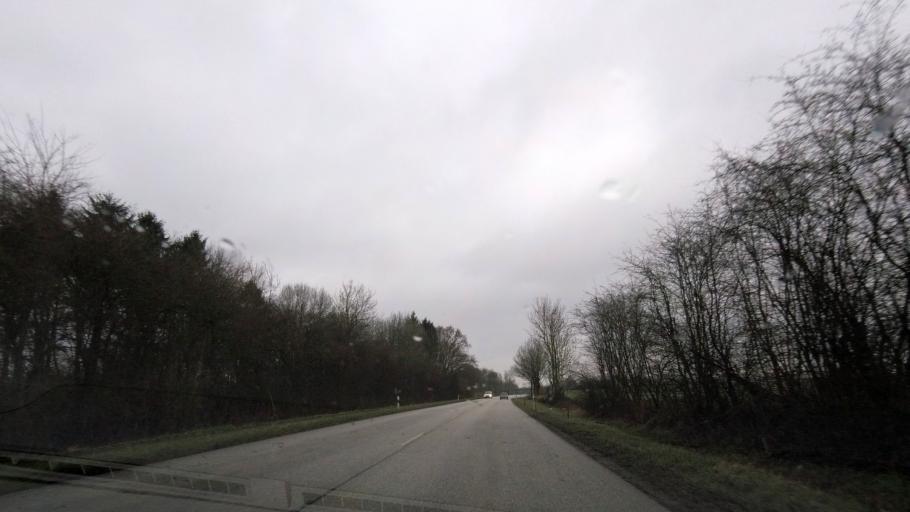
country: DE
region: Schleswig-Holstein
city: Kirchbarkau
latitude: 54.2188
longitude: 10.1466
